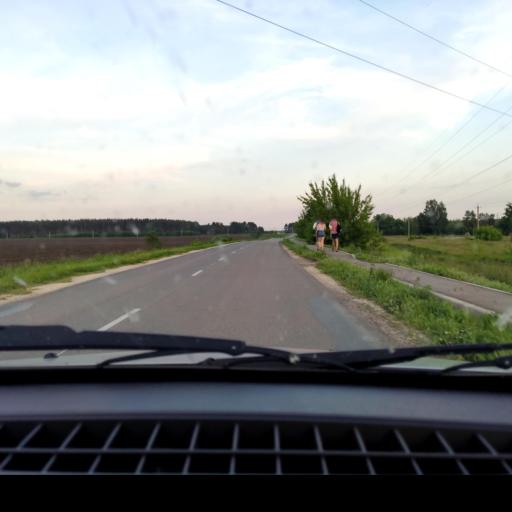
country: RU
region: Voronezj
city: Ramon'
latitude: 51.9622
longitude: 39.3946
